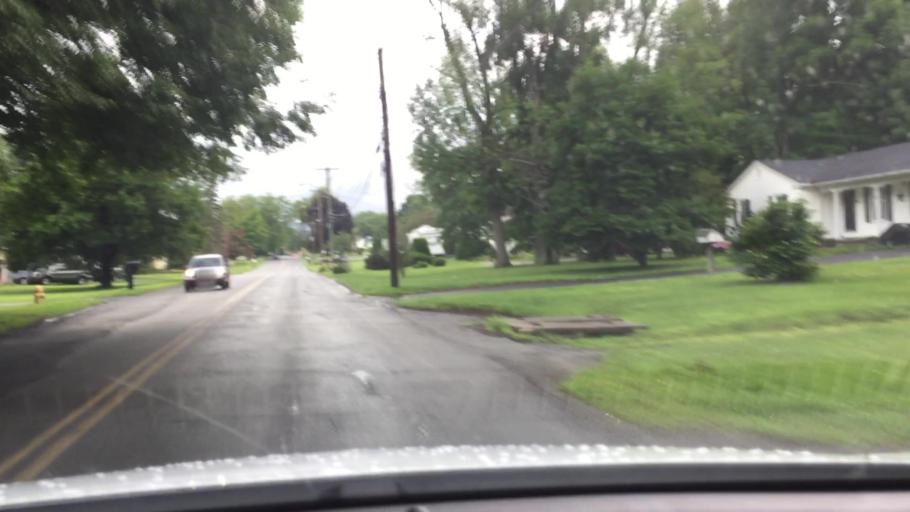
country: US
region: Massachusetts
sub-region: Berkshire County
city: Dalton
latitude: 42.4485
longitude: -73.1919
